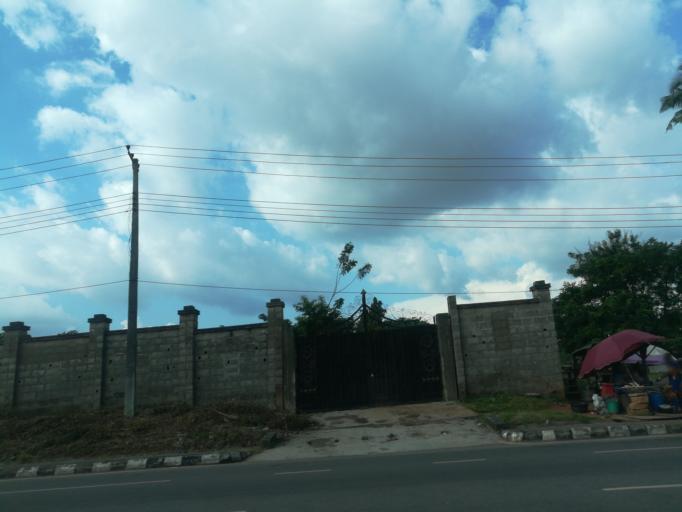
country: NG
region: Oyo
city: Ibadan
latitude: 7.3963
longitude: 3.8797
